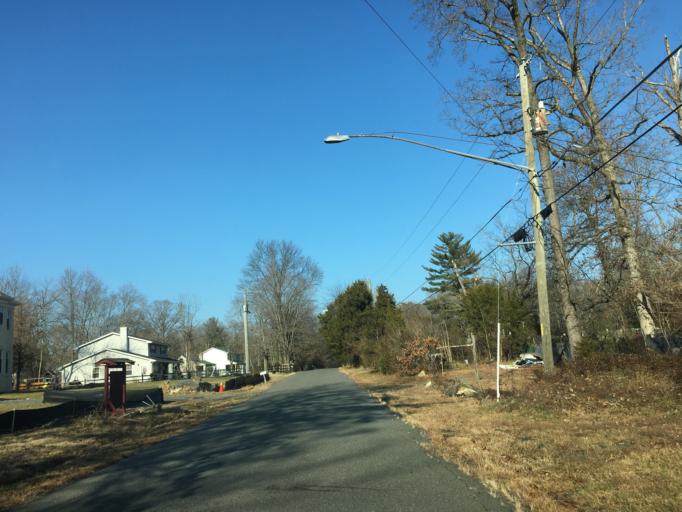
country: US
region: Virginia
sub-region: Fairfax County
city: Fairfax Station
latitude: 38.8279
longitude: -77.3711
